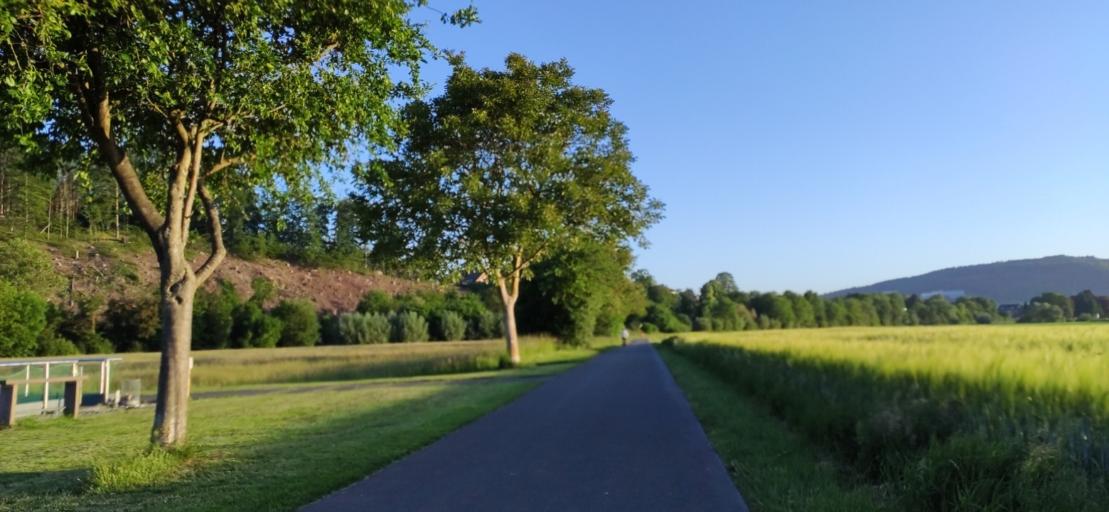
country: DE
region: North Rhine-Westphalia
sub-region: Regierungsbezirk Detmold
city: Hoexter
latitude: 51.7626
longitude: 9.3793
